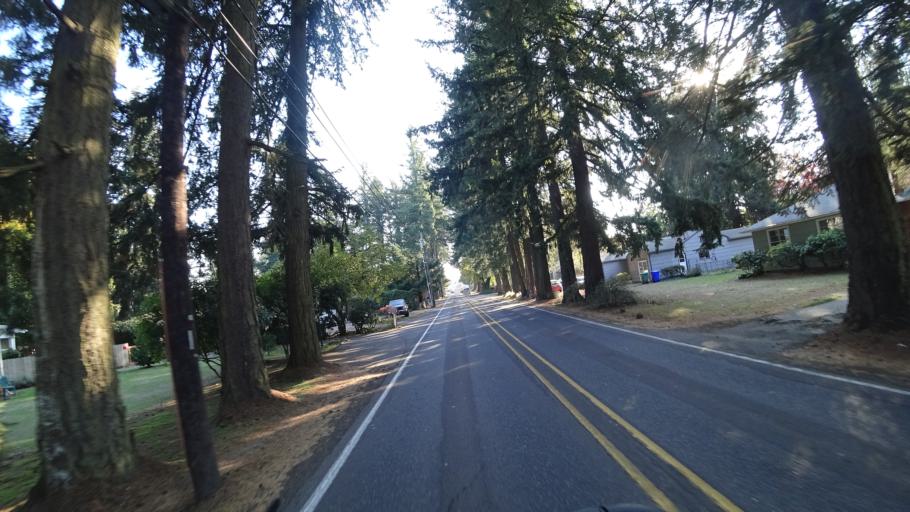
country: US
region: Oregon
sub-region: Multnomah County
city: Fairview
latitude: 45.5216
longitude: -122.4552
